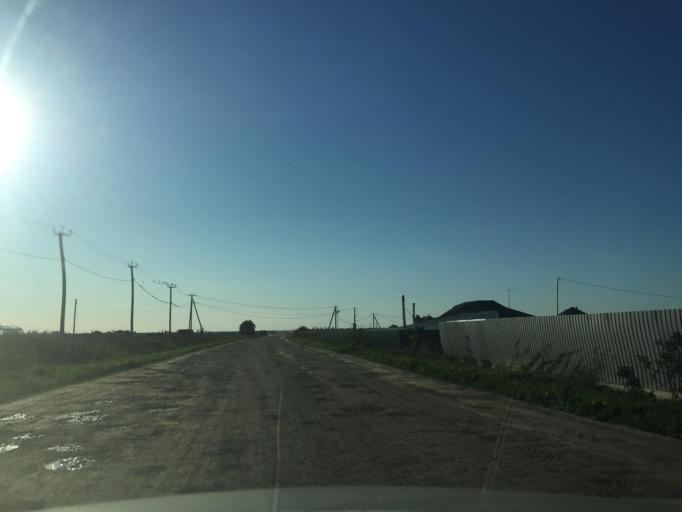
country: RU
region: Leningrad
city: Siverskiy
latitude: 59.3299
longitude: 30.0226
